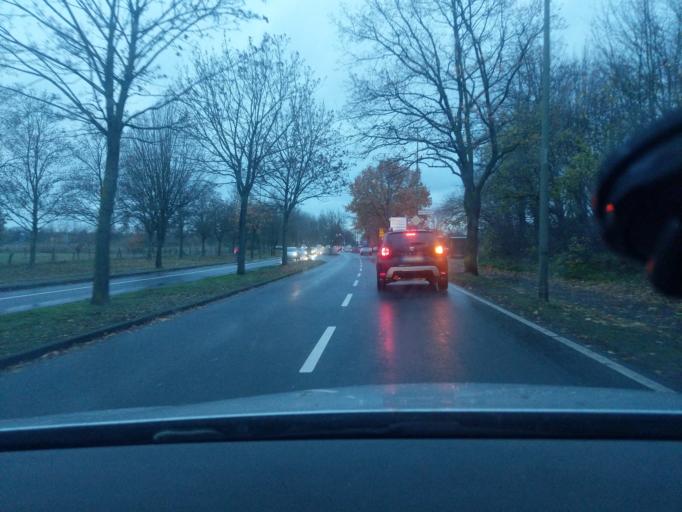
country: DE
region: North Rhine-Westphalia
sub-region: Regierungsbezirk Arnsberg
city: Hamm
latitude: 51.6694
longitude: 7.8506
